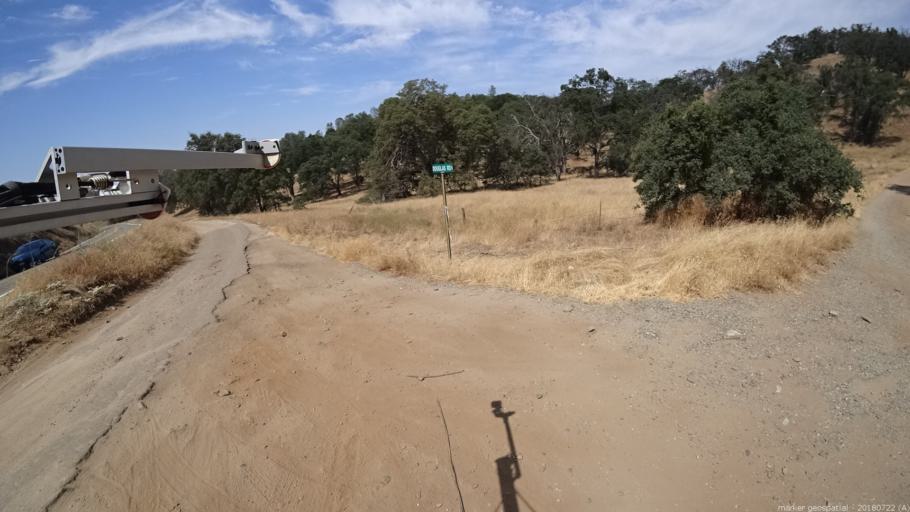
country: US
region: California
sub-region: Madera County
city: Coarsegold
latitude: 37.2624
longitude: -119.7147
